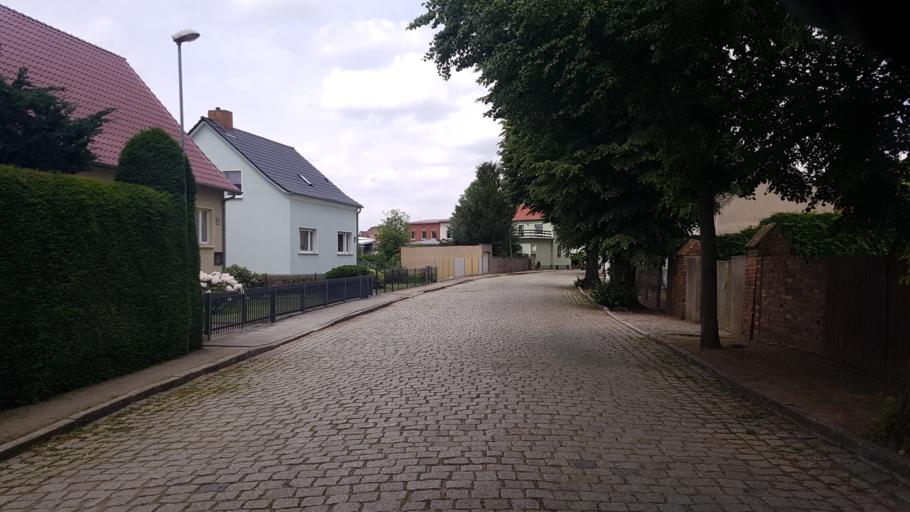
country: DE
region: Brandenburg
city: Dahme
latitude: 51.8673
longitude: 13.4249
